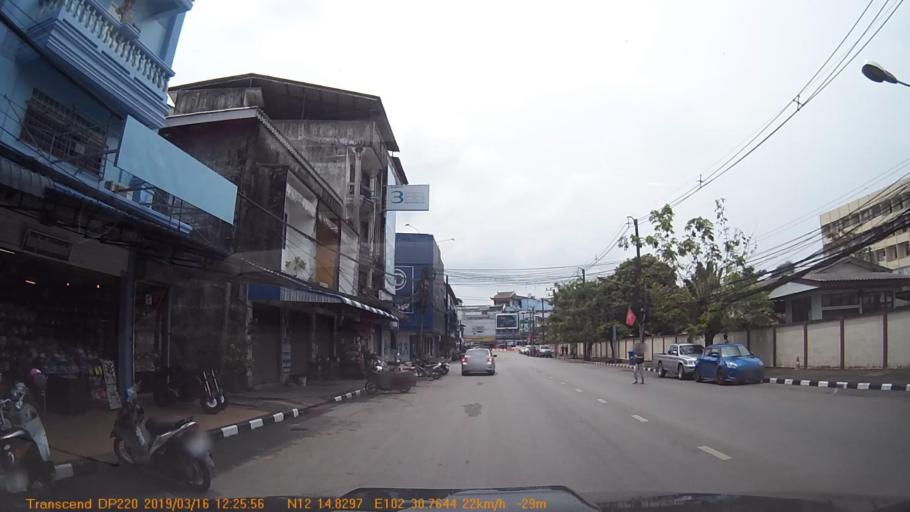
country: TH
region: Trat
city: Trat
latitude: 12.2471
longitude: 102.5127
